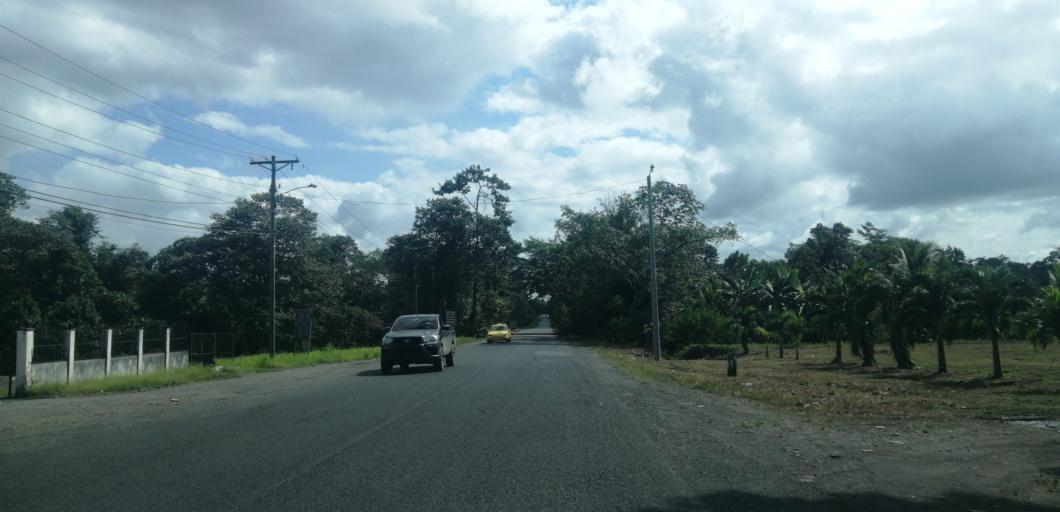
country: PA
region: Panama
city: Canita
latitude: 9.2214
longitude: -78.8888
